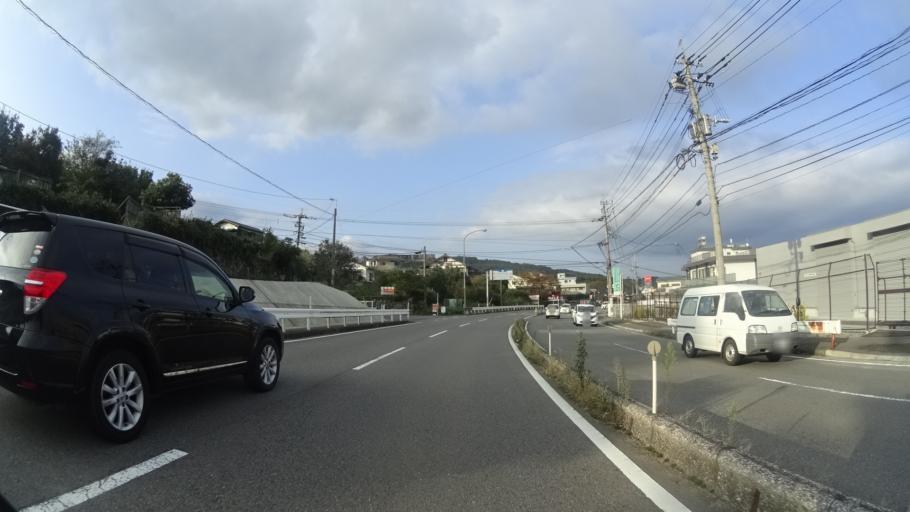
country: JP
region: Oita
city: Beppu
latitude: 33.3057
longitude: 131.4614
